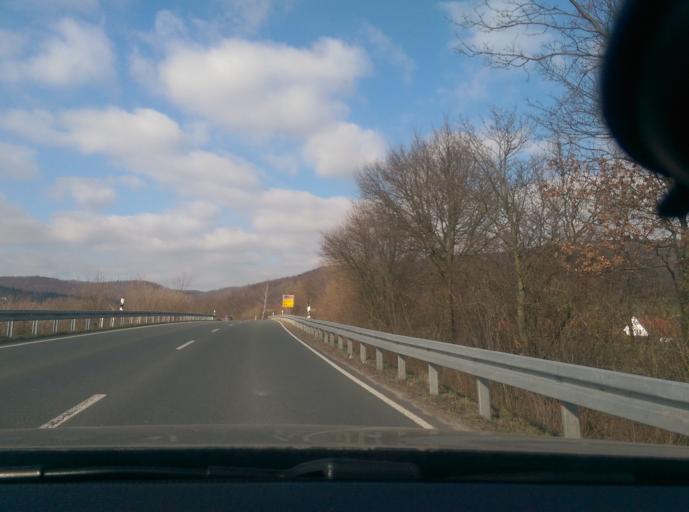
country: DE
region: Lower Saxony
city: Hessisch Oldendorf
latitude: 52.1884
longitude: 9.2501
